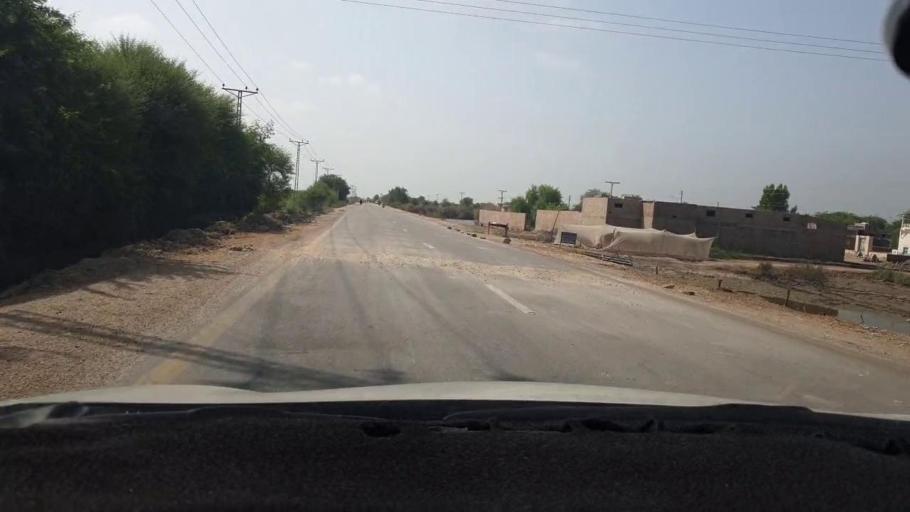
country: PK
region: Sindh
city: Tando Mittha Khan
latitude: 25.7762
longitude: 69.0713
